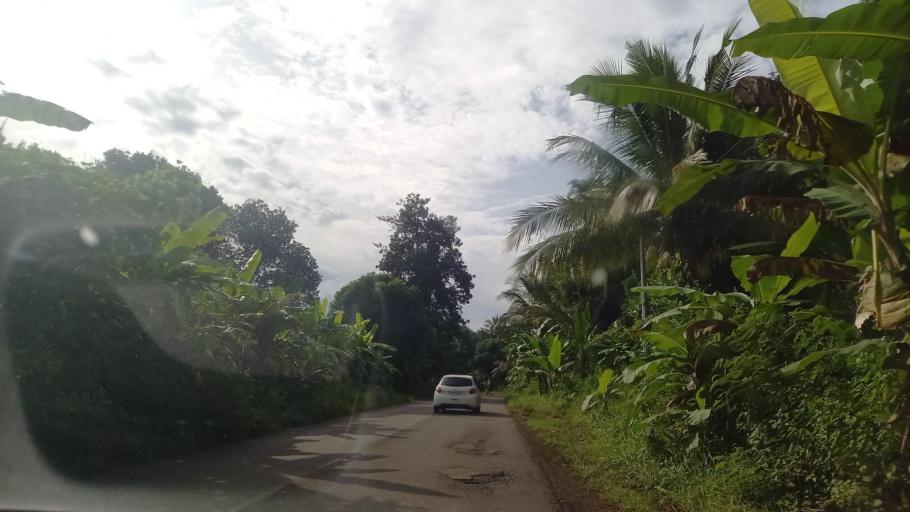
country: YT
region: Ouangani
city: Ouangani
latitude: -12.8764
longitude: 45.1227
